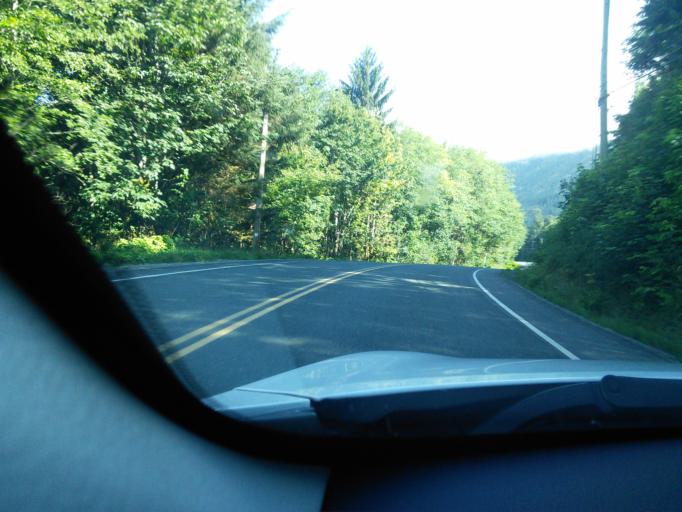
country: CA
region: British Columbia
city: Campbell River
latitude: 50.3442
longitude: -125.9070
